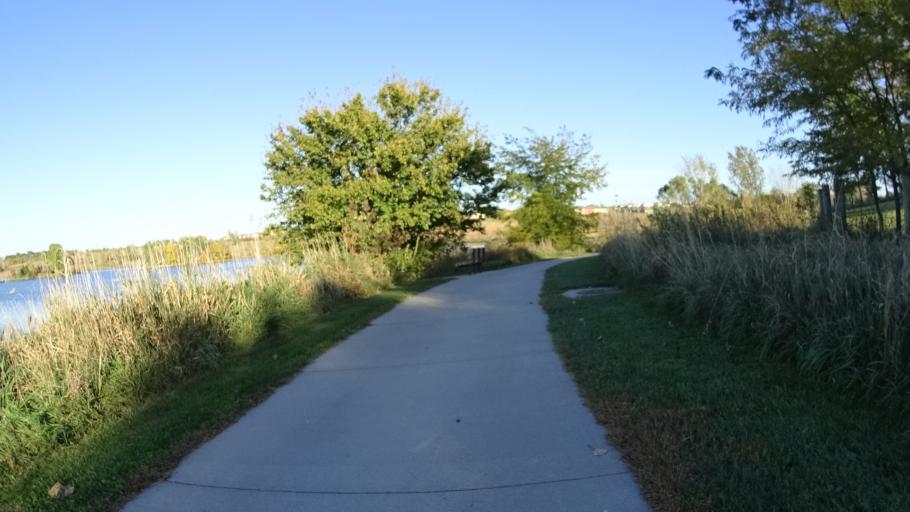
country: US
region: Nebraska
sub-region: Sarpy County
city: Papillion
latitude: 41.1349
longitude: -96.0698
